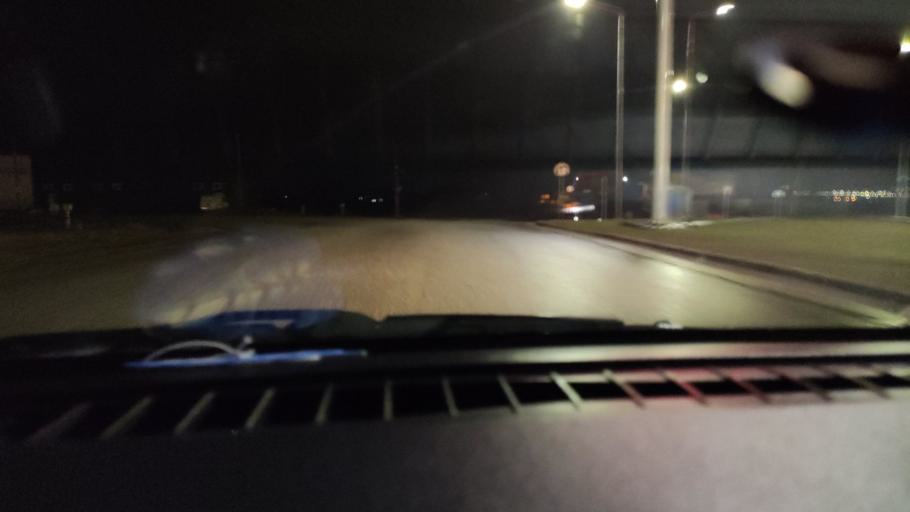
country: RU
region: Udmurtiya
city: Votkinsk
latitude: 57.0296
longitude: 53.9503
